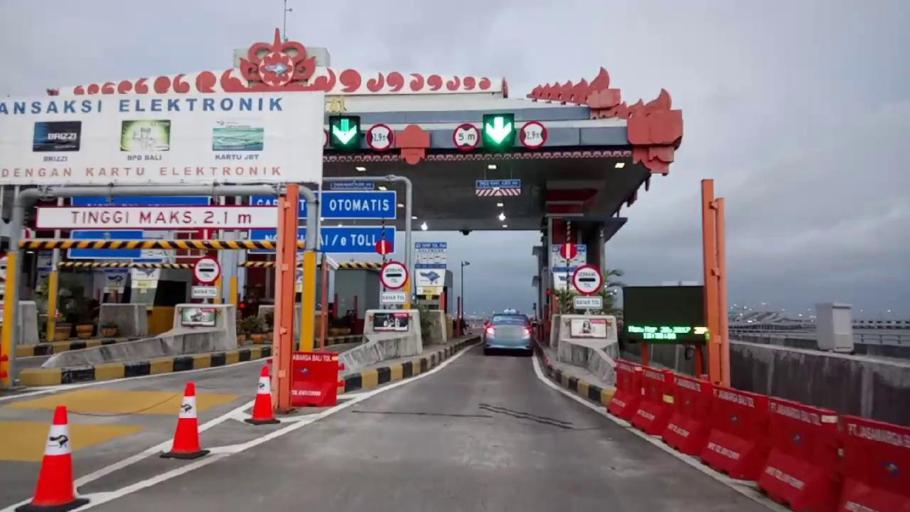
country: ID
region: Bali
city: Kelanabian
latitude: -8.7445
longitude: 115.1880
